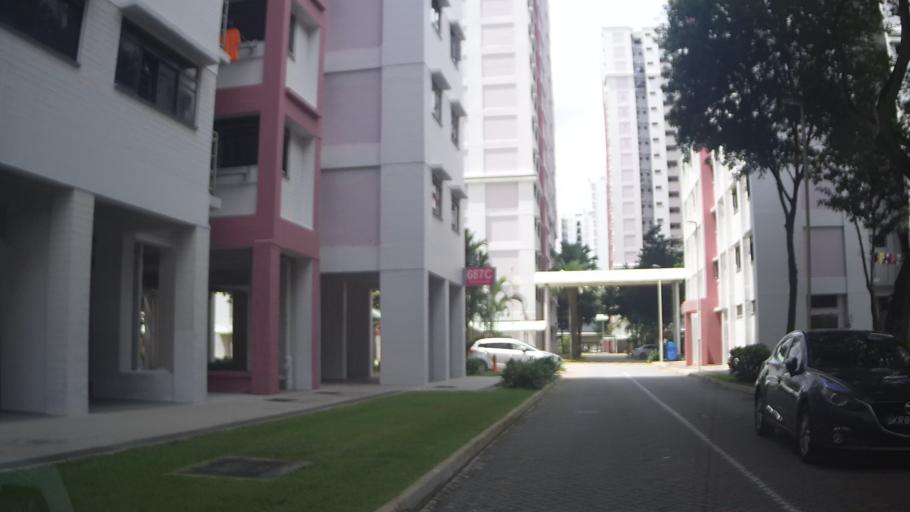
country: MY
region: Johor
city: Johor Bahru
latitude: 1.4040
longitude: 103.7513
